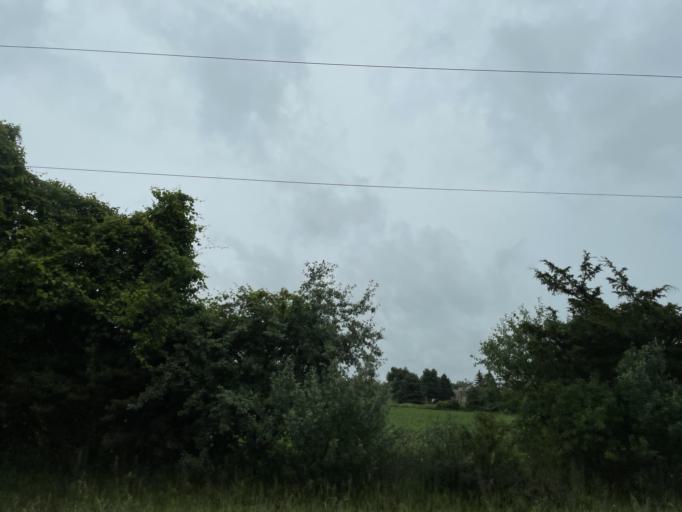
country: CA
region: Ontario
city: Cambridge
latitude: 43.4322
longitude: -80.2610
